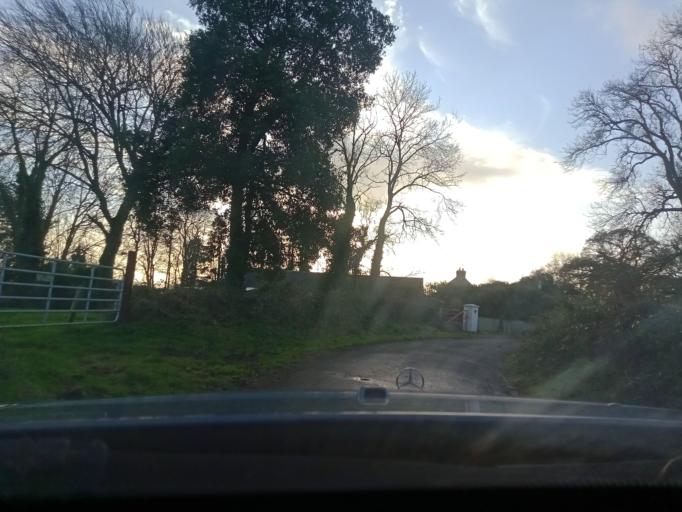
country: IE
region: Leinster
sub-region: Kilkenny
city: Callan
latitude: 52.4491
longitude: -7.4175
